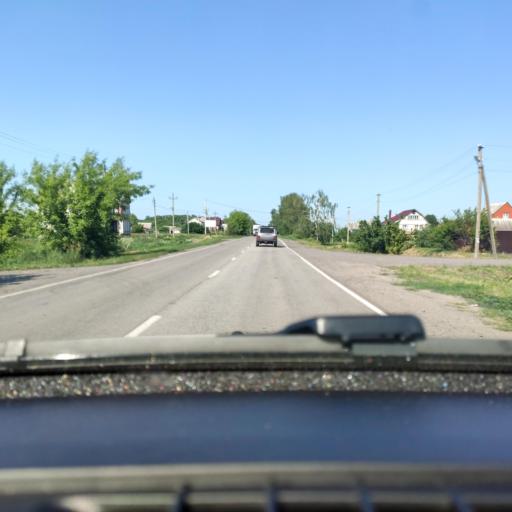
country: RU
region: Voronezj
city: Panino
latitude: 51.6512
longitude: 40.1150
